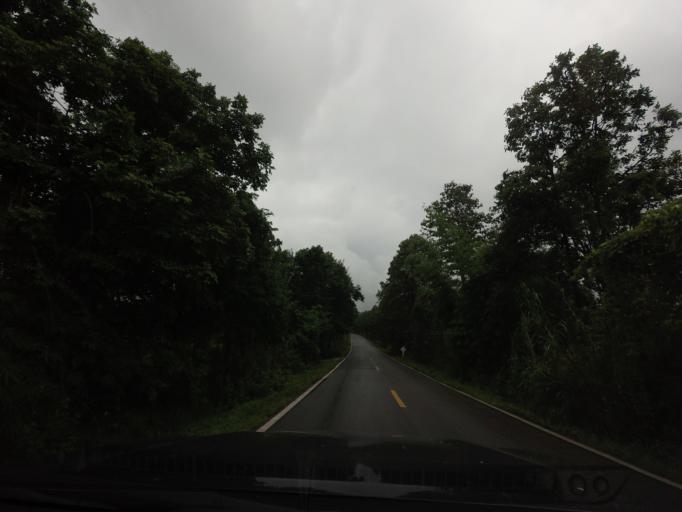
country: TH
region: Nong Khai
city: Sangkhom
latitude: 18.0317
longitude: 102.3403
